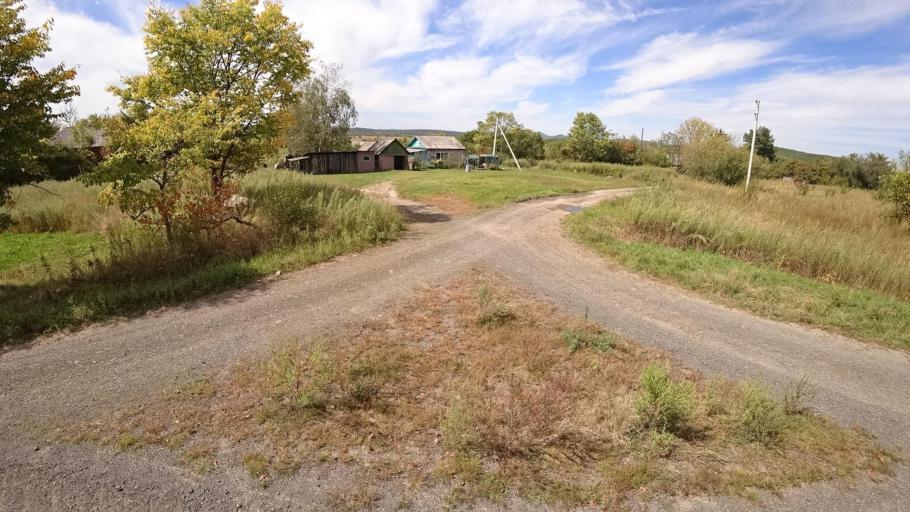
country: RU
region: Primorskiy
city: Yakovlevka
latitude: 44.6420
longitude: 133.5882
